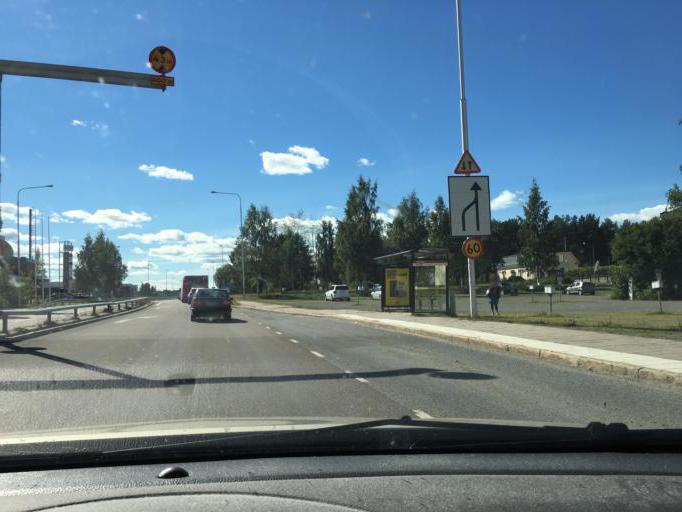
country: SE
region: Norrbotten
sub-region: Lulea Kommun
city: Lulea
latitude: 65.5804
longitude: 22.1370
